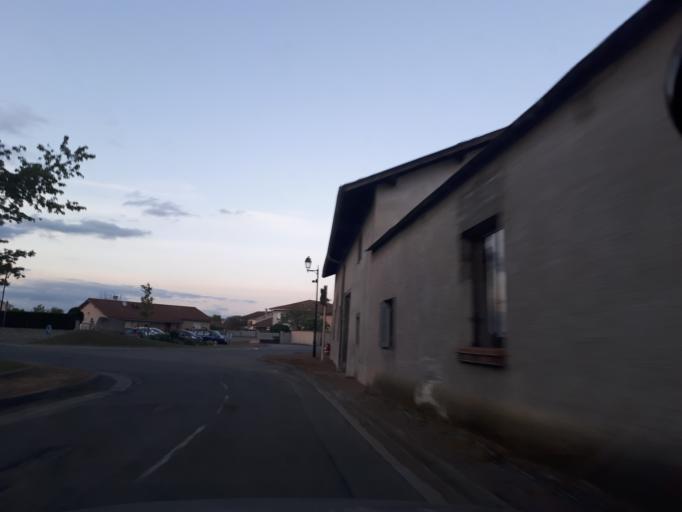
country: FR
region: Rhone-Alpes
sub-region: Departement de la Loire
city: Montrond-les-Bains
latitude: 45.6840
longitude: 4.2088
